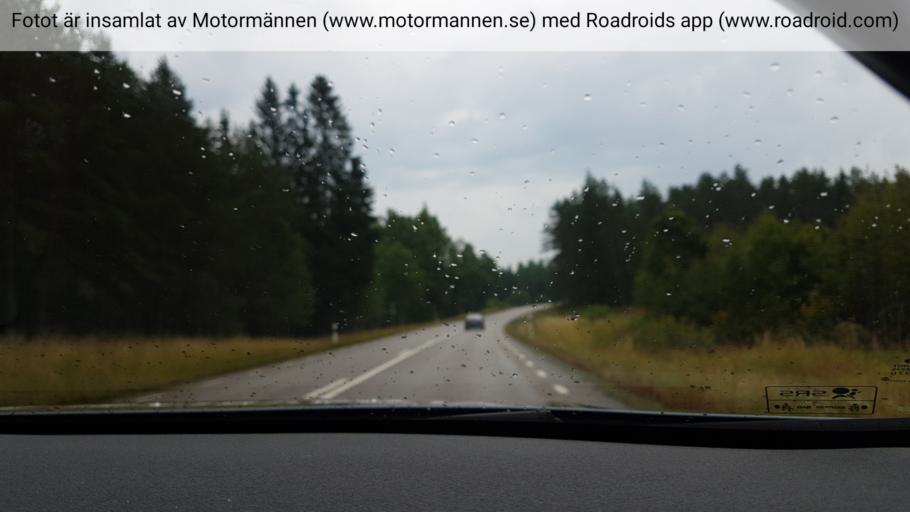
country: SE
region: Joenkoeping
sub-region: Vaggeryds Kommun
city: Vaggeryd
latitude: 57.5345
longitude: 14.2710
